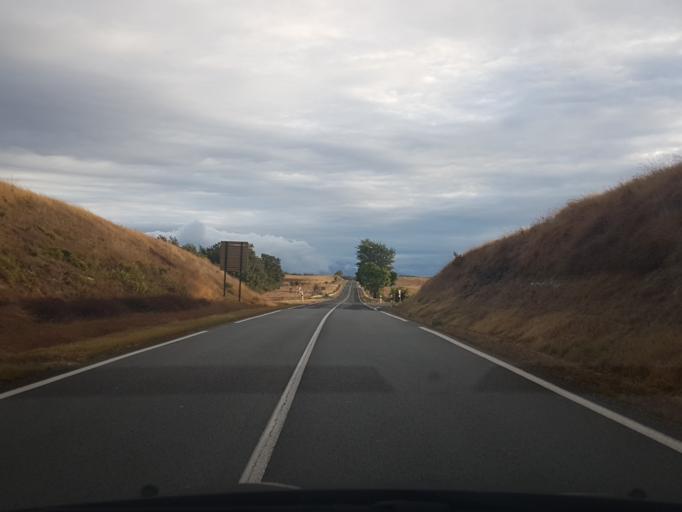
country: FR
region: Languedoc-Roussillon
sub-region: Departement de l'Aude
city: Saint-Martin-Lalande
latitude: 43.1653
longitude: 1.9946
